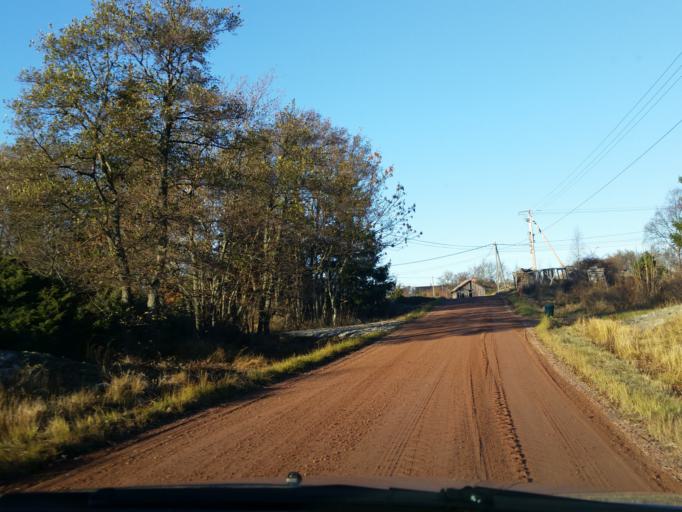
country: AX
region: Alands skaergard
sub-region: Braendoe
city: Braendoe
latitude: 60.4492
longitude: 20.9377
